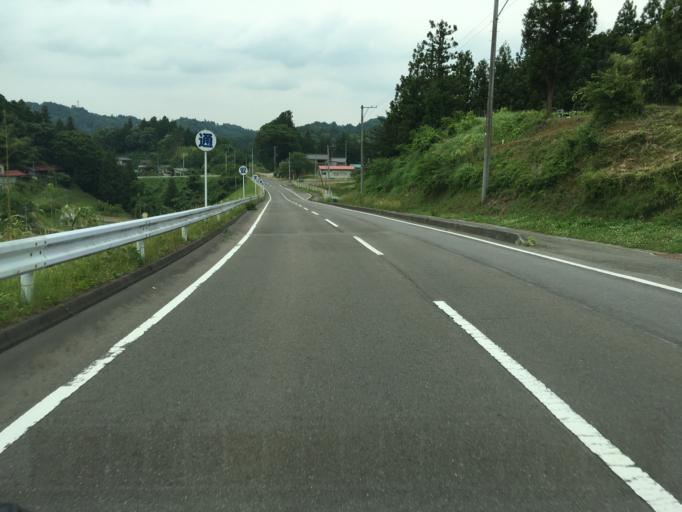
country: JP
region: Fukushima
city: Nihommatsu
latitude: 37.6110
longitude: 140.5600
